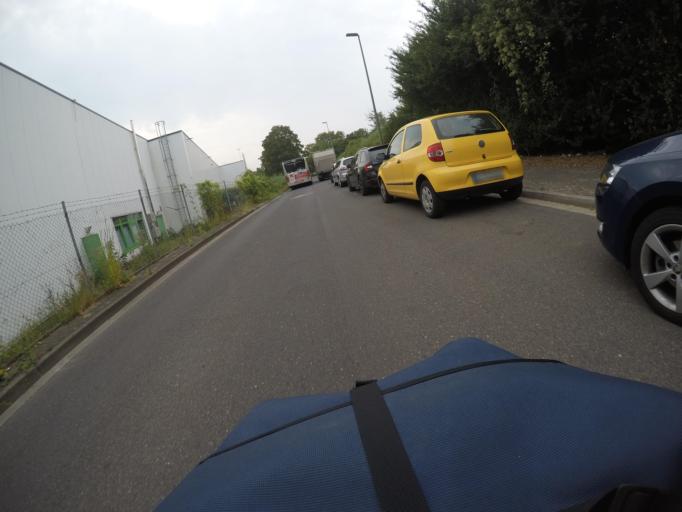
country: DE
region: North Rhine-Westphalia
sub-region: Regierungsbezirk Dusseldorf
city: Neuss
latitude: 51.2058
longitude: 6.7177
